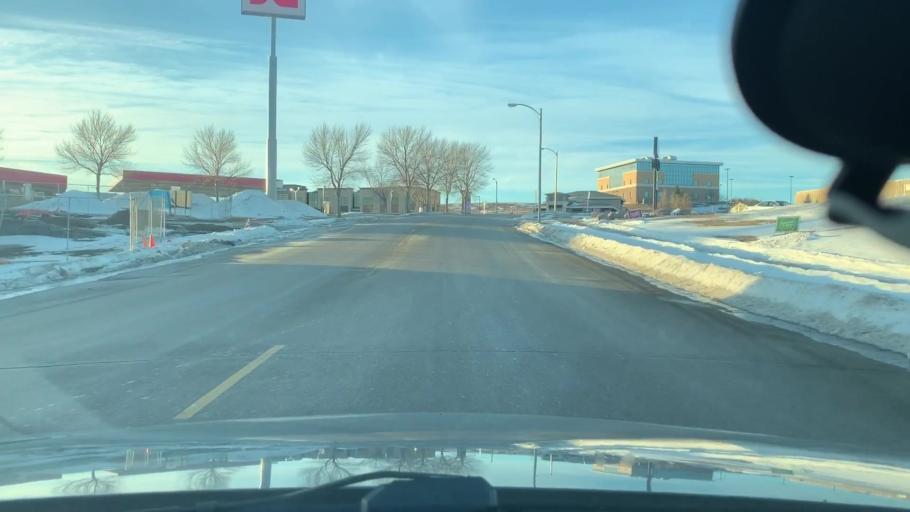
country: US
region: North Dakota
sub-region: Burleigh County
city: Bismarck
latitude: 46.8262
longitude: -100.8113
